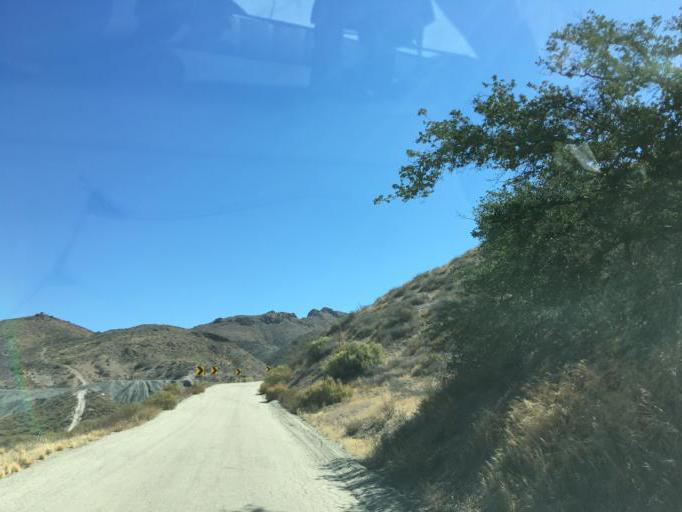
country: US
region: California
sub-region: Los Angeles County
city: Agua Dulce
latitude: 34.4760
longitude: -118.3662
